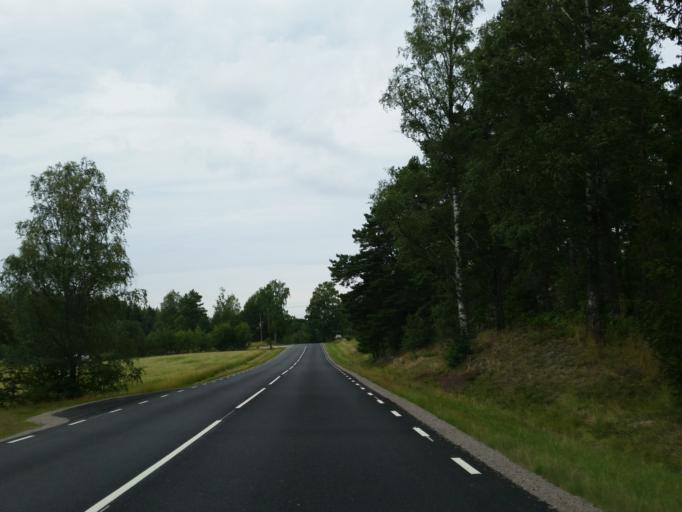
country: SE
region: Soedermanland
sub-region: Strangnas Kommun
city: Mariefred
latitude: 59.2704
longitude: 17.1543
